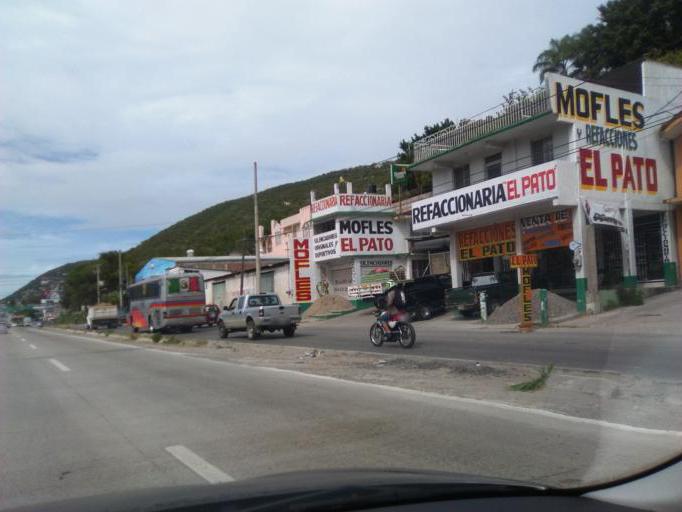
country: MX
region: Guerrero
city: Chilpancingo de los Bravos
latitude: 17.5724
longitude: -99.5127
